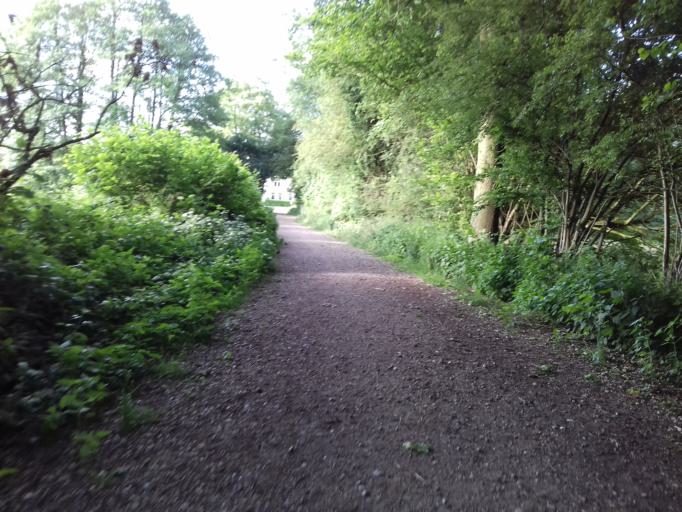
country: DE
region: Schleswig-Holstein
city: Tasdorf
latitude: 54.0799
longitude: 10.0149
